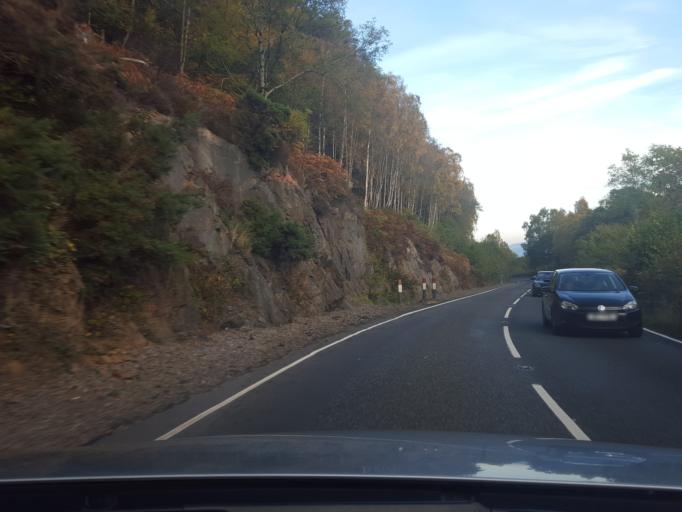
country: GB
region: Scotland
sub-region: Highland
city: Beauly
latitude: 57.3484
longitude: -4.4144
